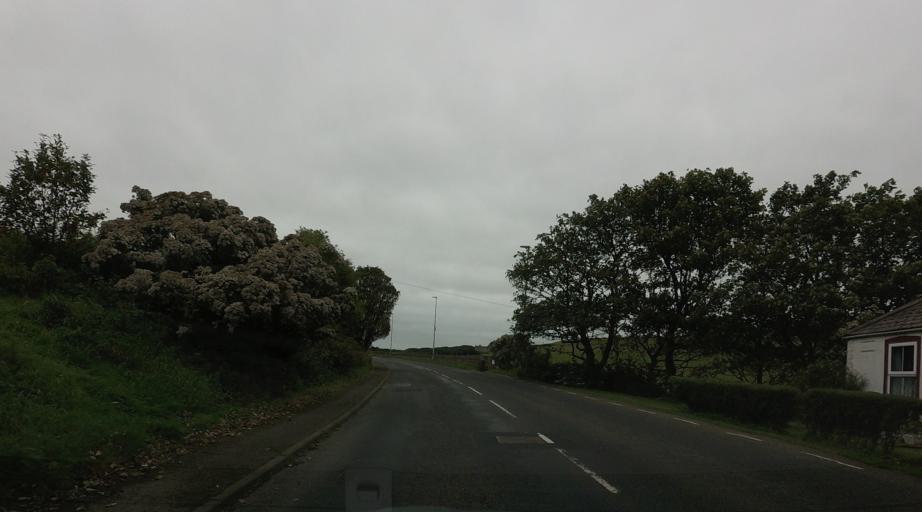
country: GB
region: Scotland
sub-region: Orkney Islands
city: Orkney
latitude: 59.0085
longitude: -3.1242
